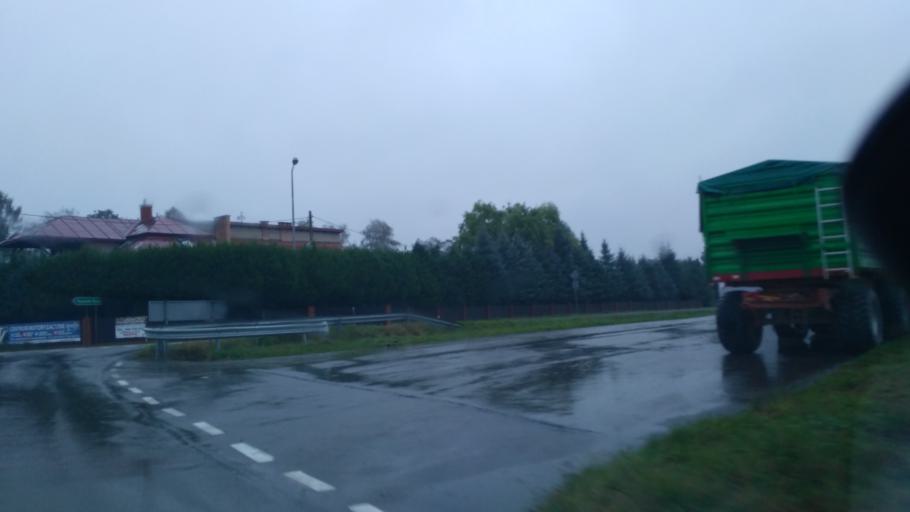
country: PL
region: Subcarpathian Voivodeship
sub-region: Powiat krosnienski
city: Korczyna
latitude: 49.7114
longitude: 21.8136
